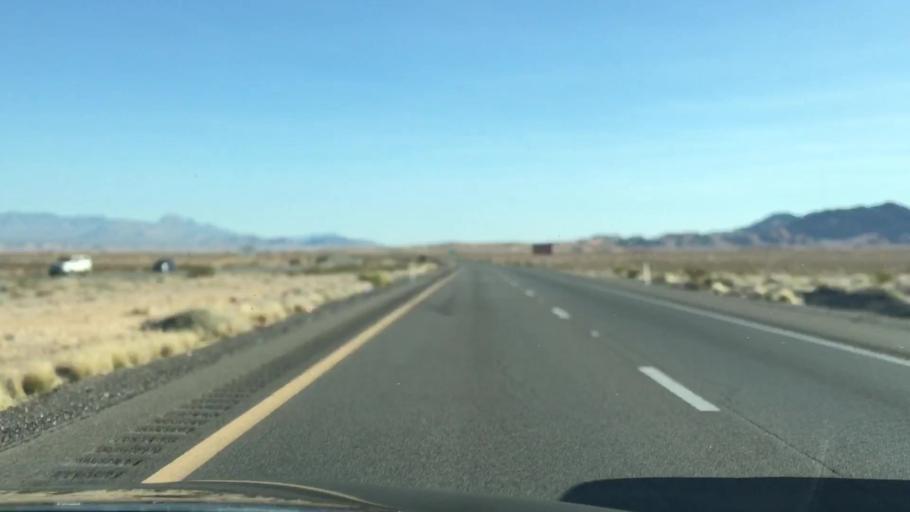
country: US
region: Nevada
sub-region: Clark County
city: Moapa Town
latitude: 36.5785
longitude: -114.6584
